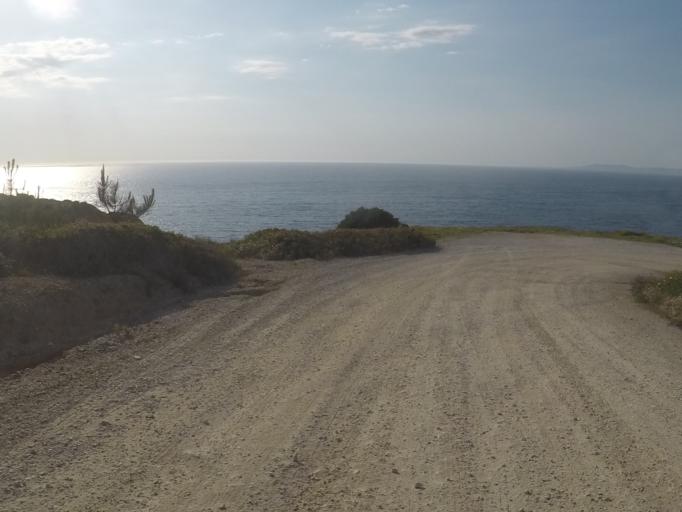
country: PT
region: Setubal
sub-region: Sesimbra
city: Sesimbra
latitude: 38.4489
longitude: -9.2003
